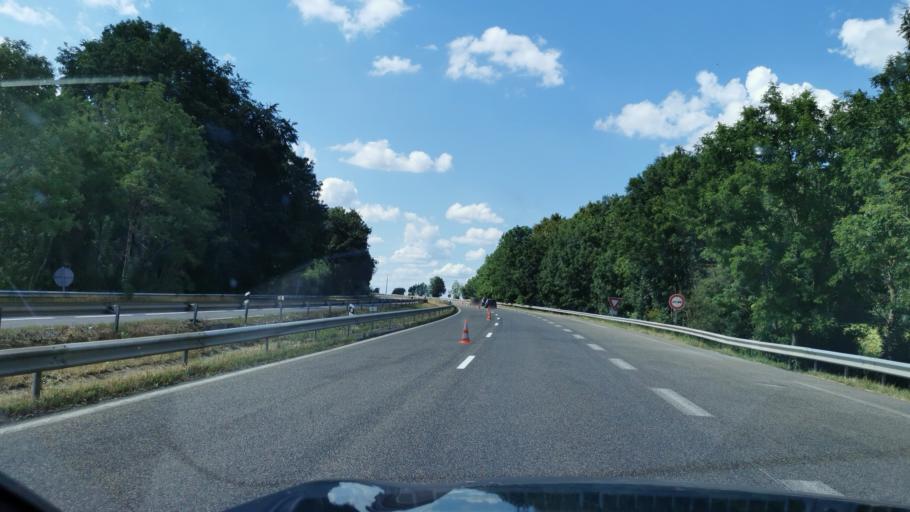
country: FR
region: Lorraine
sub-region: Departement de Meurthe-et-Moselle
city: Villers-la-Montagne
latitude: 49.4736
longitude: 5.8344
